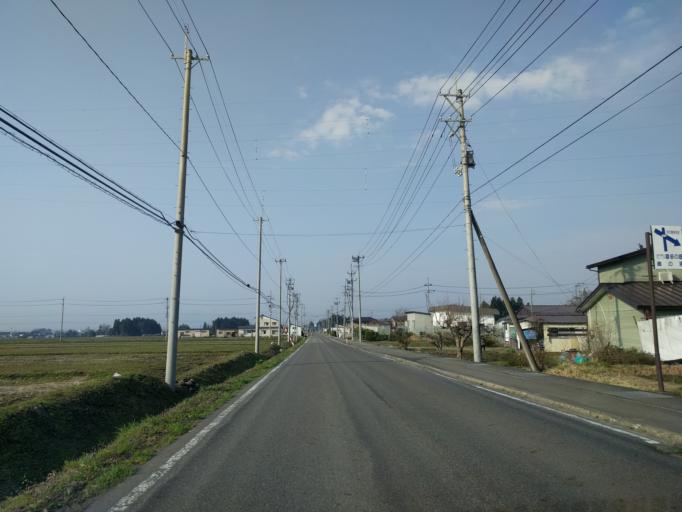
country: JP
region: Fukushima
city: Kitakata
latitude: 37.6747
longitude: 139.8928
